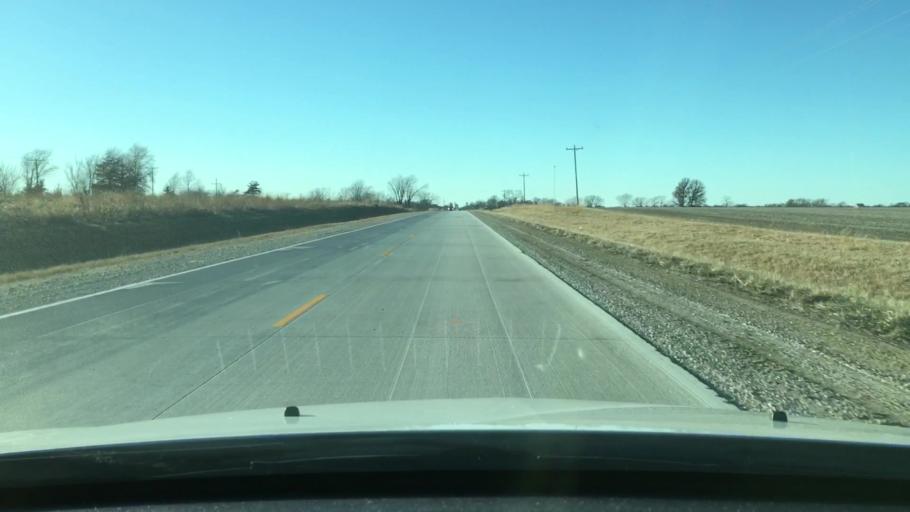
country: US
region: Missouri
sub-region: Boone County
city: Centralia
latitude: 39.2032
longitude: -92.0760
